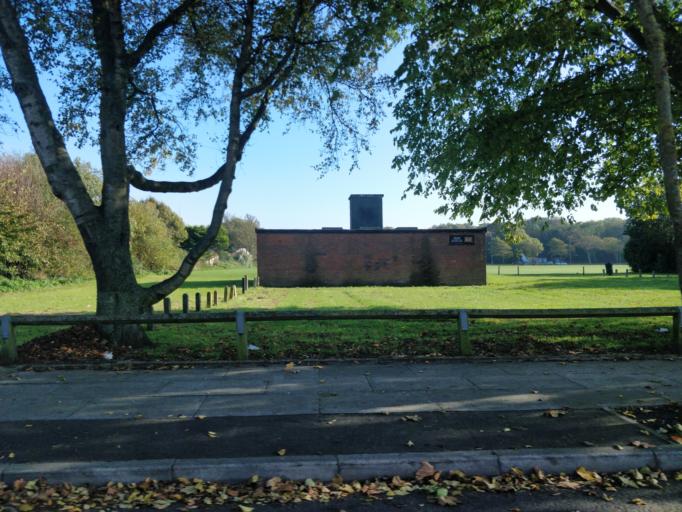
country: GB
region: England
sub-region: Lancashire
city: Banks
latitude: 53.6705
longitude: -2.9603
